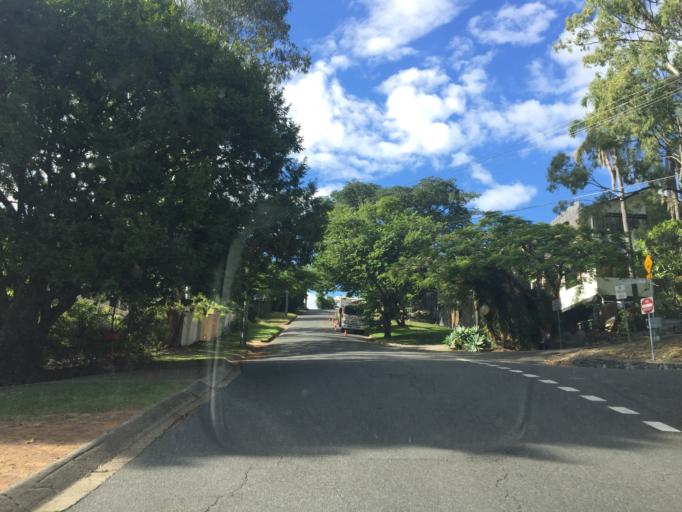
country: AU
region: Queensland
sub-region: Brisbane
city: Milton
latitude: -27.4554
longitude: 152.9890
